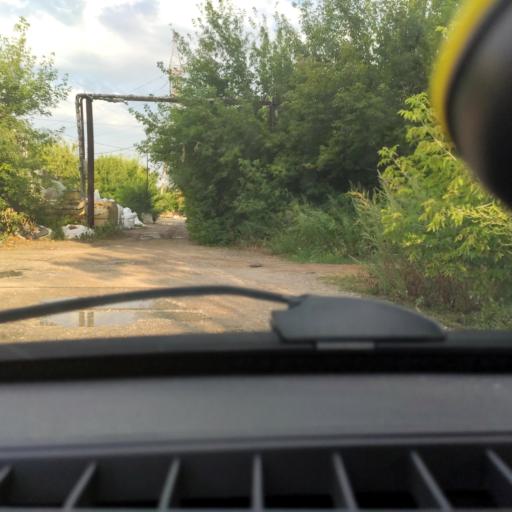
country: RU
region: Samara
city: Tol'yatti
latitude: 53.5709
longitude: 49.3001
